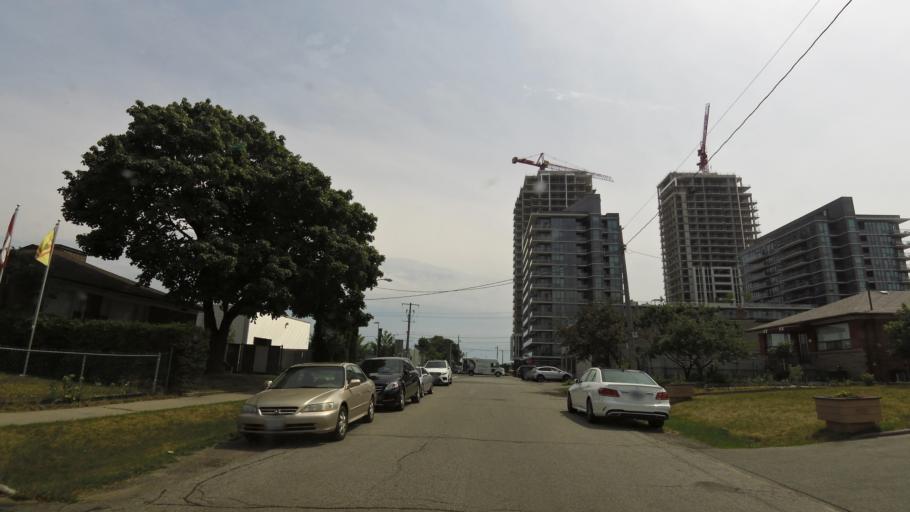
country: CA
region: Ontario
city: Etobicoke
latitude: 43.6230
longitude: -79.5213
